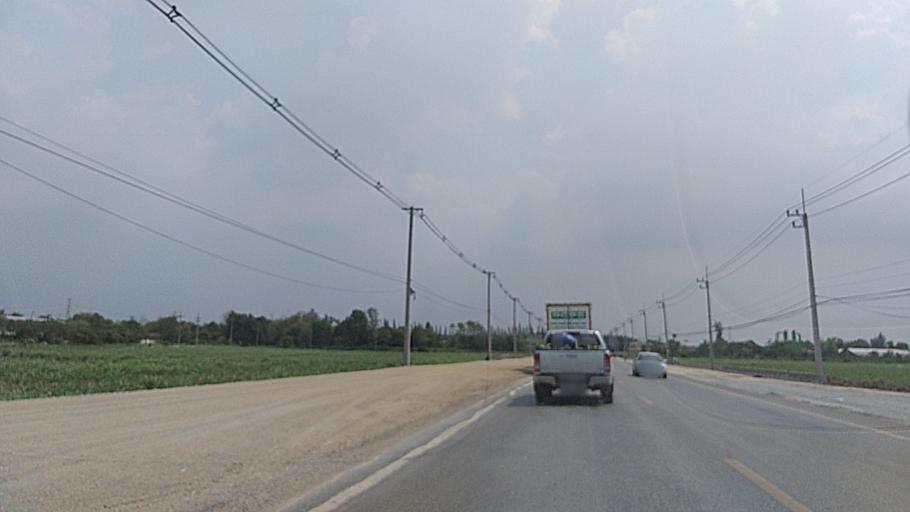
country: TH
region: Chon Buri
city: Phanat Nikhom
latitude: 13.3668
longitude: 101.1959
